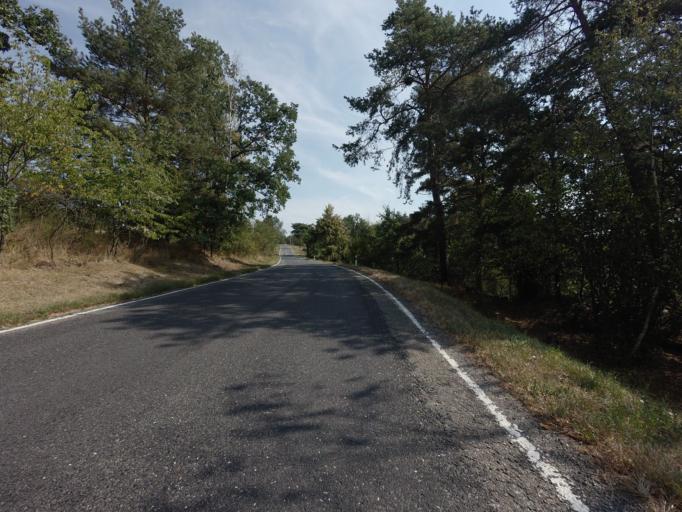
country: CZ
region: Central Bohemia
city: Petrovice
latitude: 49.5682
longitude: 14.3671
